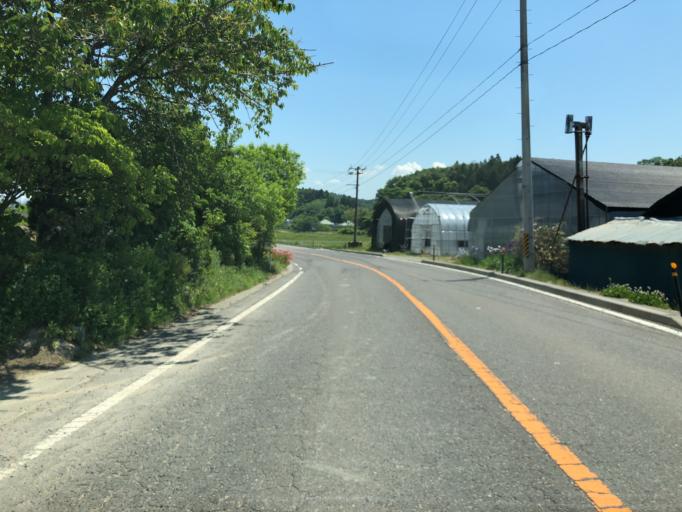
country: JP
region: Fukushima
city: Motomiya
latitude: 37.5005
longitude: 140.4603
